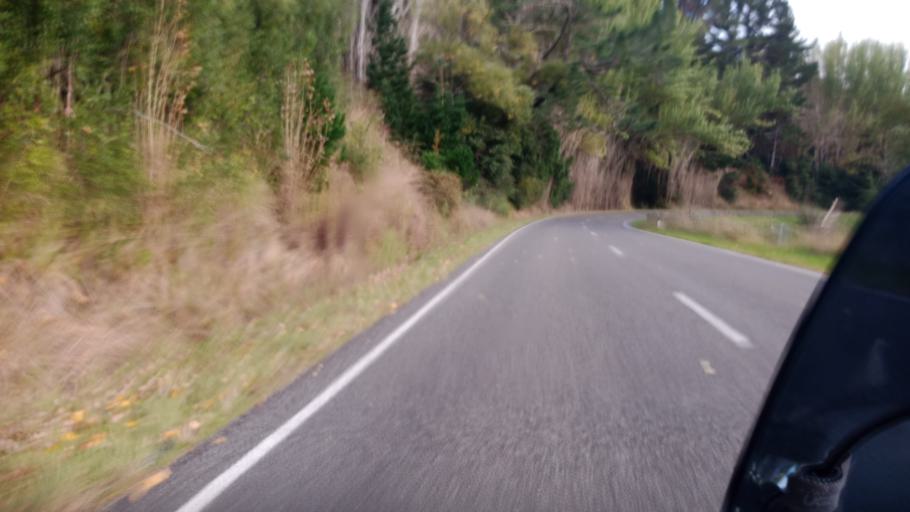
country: NZ
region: Gisborne
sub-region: Gisborne District
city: Gisborne
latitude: -38.5679
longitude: 177.7231
